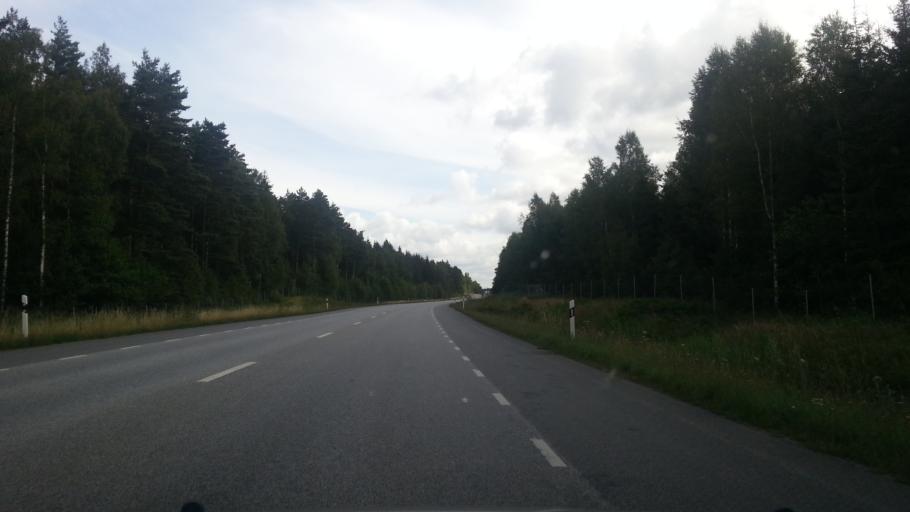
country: SE
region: Vaestra Goetaland
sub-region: Mariestads Kommun
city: Mariestad
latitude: 58.6341
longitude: 13.6843
